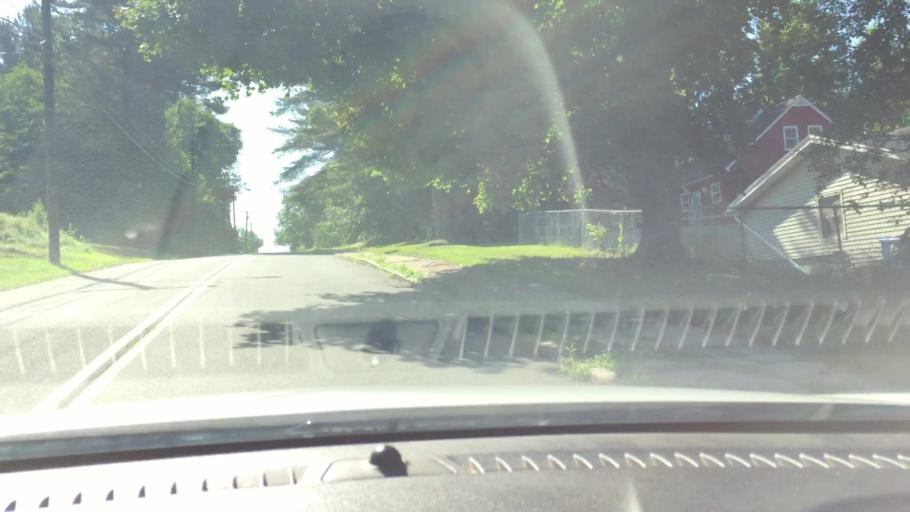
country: US
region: Massachusetts
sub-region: Berkshire County
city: Lanesborough
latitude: 42.5160
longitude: -73.2247
